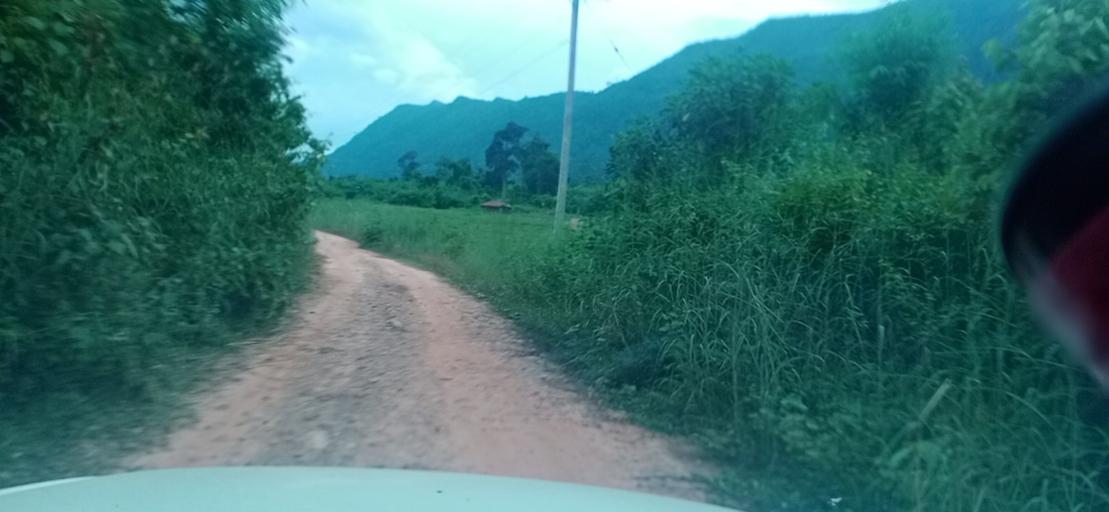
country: TH
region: Changwat Bueng Kan
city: Pak Khat
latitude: 18.5625
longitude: 103.2856
